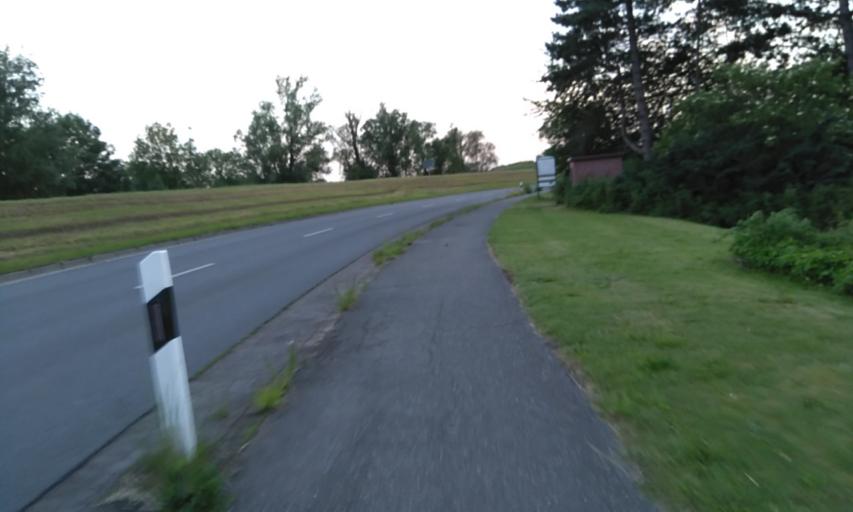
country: DE
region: Lower Saxony
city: Buxtehude
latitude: 53.4957
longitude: 9.7168
